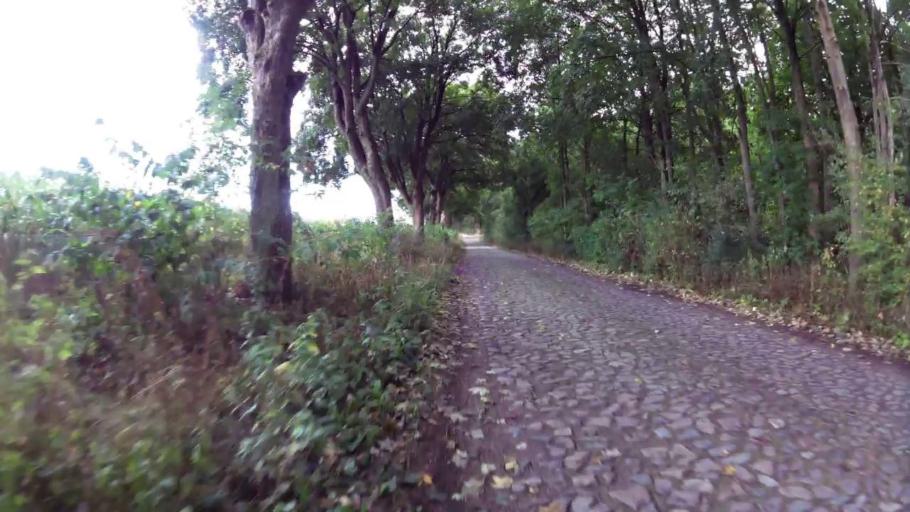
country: PL
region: West Pomeranian Voivodeship
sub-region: Powiat mysliborski
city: Debno
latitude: 52.8487
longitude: 14.7117
